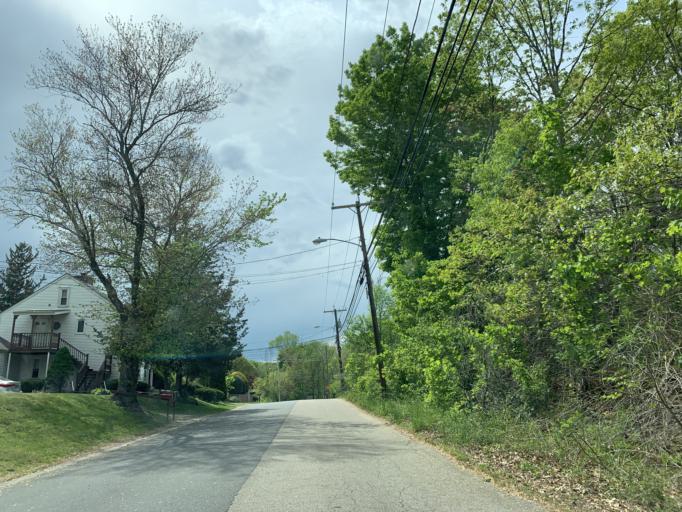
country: US
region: Rhode Island
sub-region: Providence County
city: Johnston
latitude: 41.8053
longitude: -71.4857
